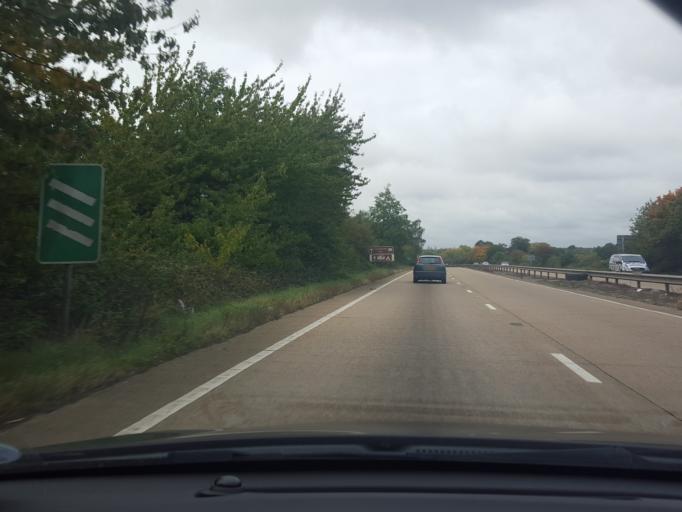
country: GB
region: England
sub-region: Essex
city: Colchester
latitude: 51.9168
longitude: 0.9445
